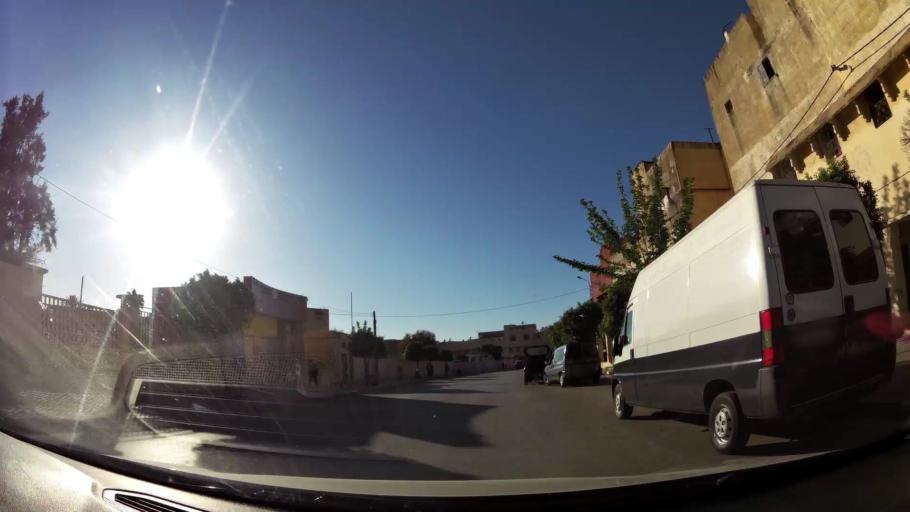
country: MA
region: Meknes-Tafilalet
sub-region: Meknes
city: Meknes
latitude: 33.8814
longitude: -5.5630
